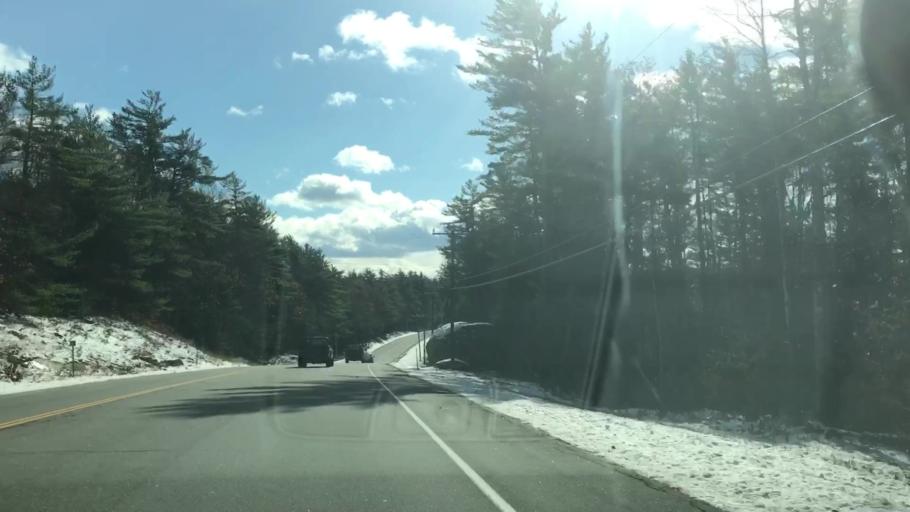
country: US
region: New Hampshire
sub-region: Carroll County
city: Ossipee
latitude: 43.7291
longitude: -71.1269
